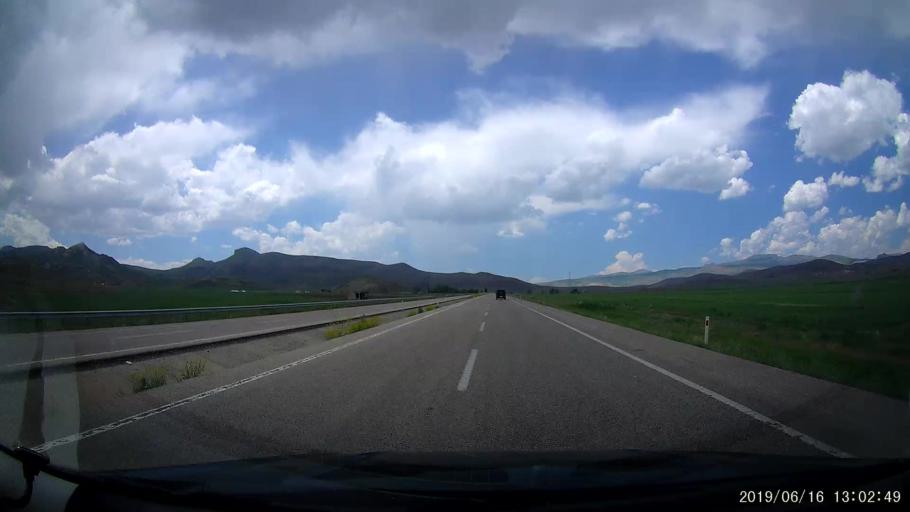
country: TR
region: Agri
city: Sulucem
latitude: 39.5768
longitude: 43.8059
